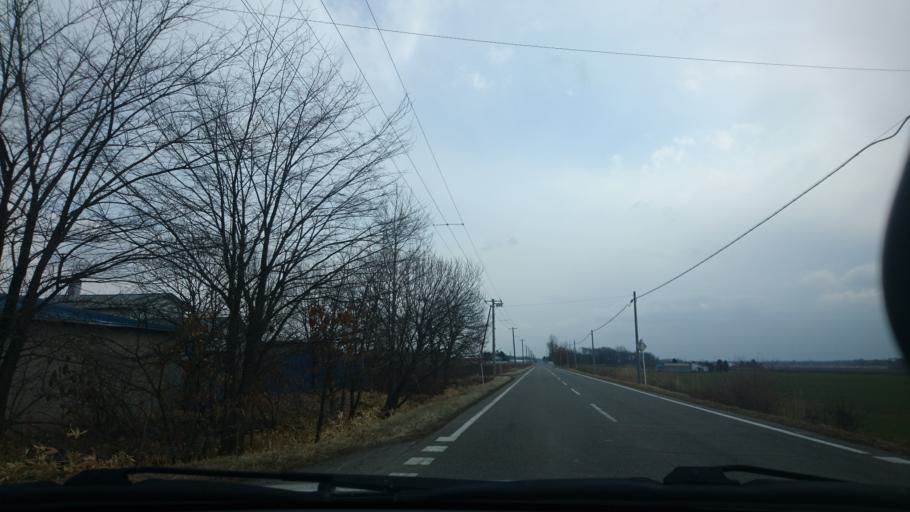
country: JP
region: Hokkaido
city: Otofuke
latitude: 43.0779
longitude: 143.2073
